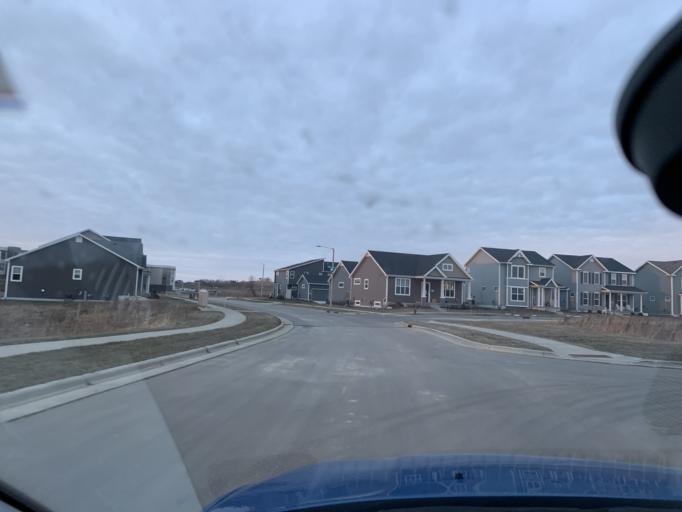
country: US
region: Wisconsin
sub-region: Dane County
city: Verona
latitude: 43.0508
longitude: -89.5576
